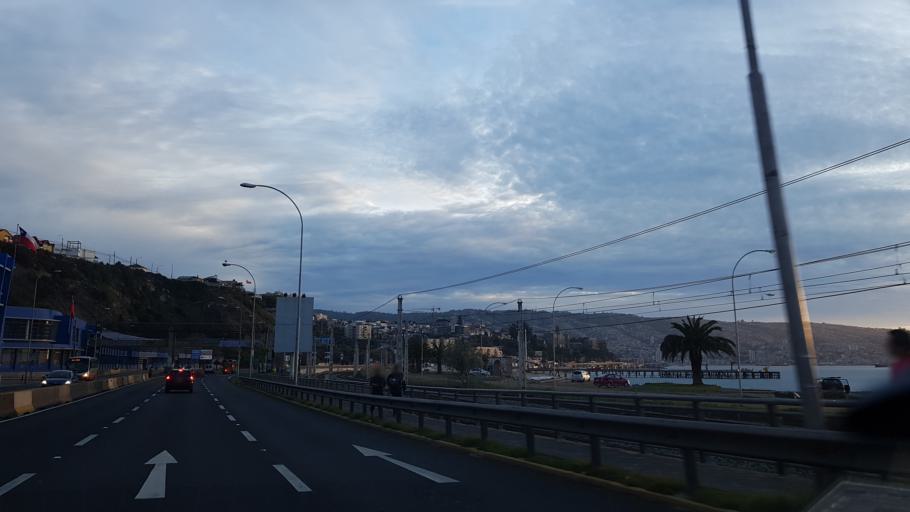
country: CL
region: Valparaiso
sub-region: Provincia de Valparaiso
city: Vina del Mar
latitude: -33.0278
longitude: -71.5860
